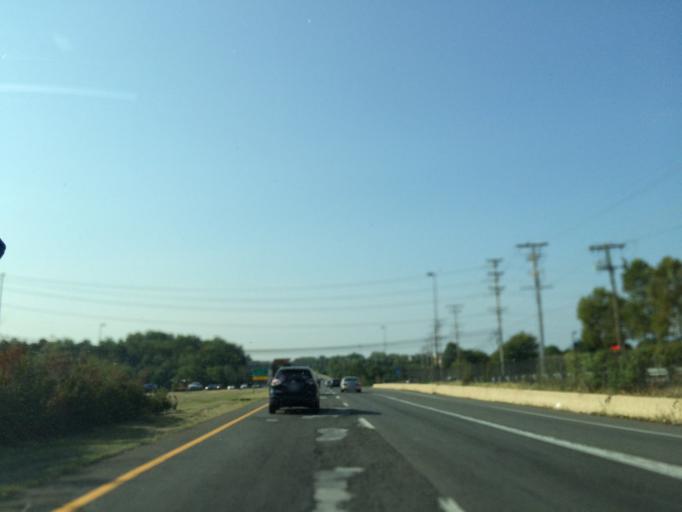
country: US
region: Maryland
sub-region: Prince George's County
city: Bowie
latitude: 38.9517
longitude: -76.7175
